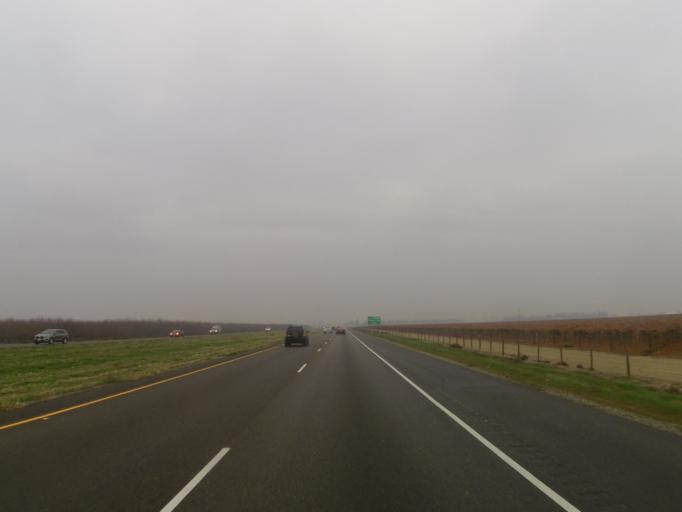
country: US
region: California
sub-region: Kern County
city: Greenfield
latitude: 35.0801
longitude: -119.0210
